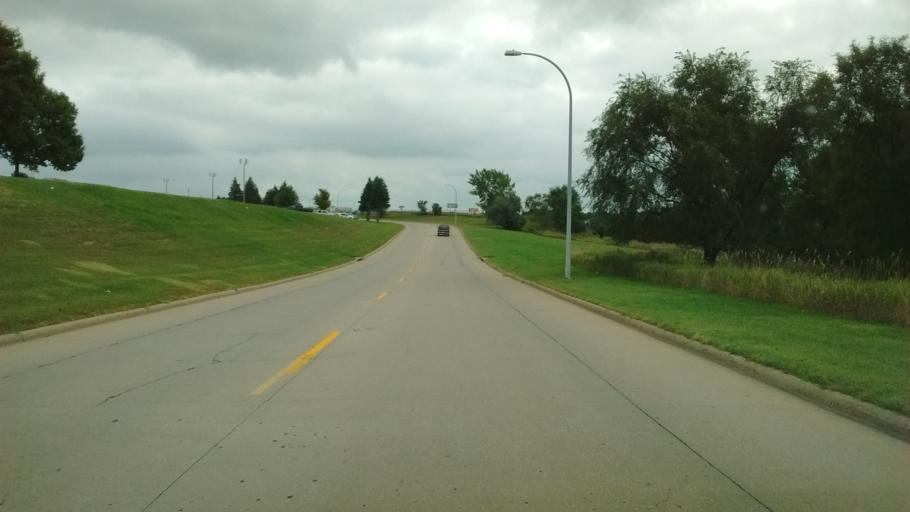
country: US
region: Iowa
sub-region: Woodbury County
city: Sergeant Bluff
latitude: 42.4462
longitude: -96.3564
